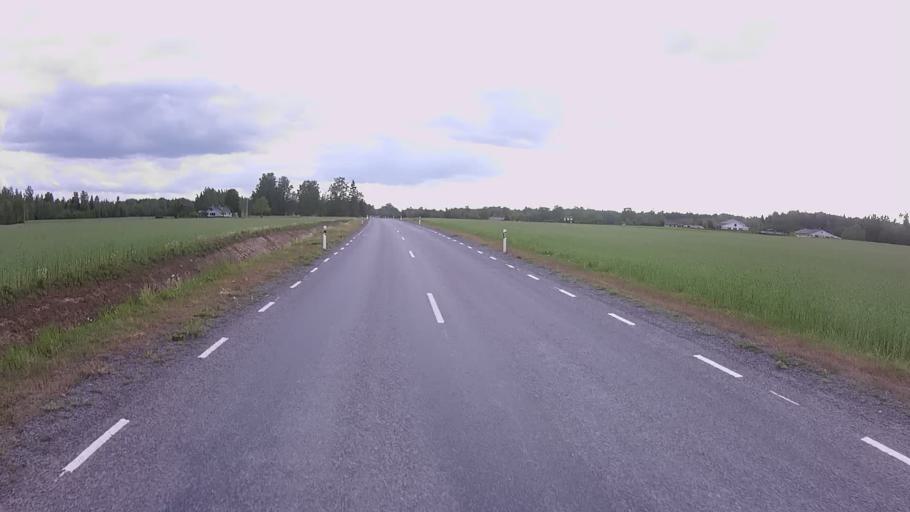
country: EE
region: Jogevamaa
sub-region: Mustvee linn
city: Mustvee
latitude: 59.0023
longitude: 26.9065
